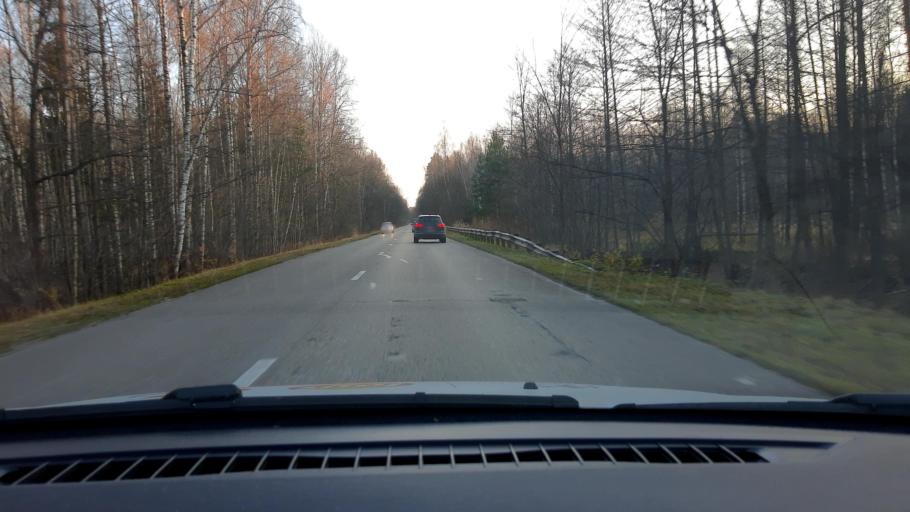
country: RU
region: Nizjnij Novgorod
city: Volodarsk
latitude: 56.2681
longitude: 43.1677
